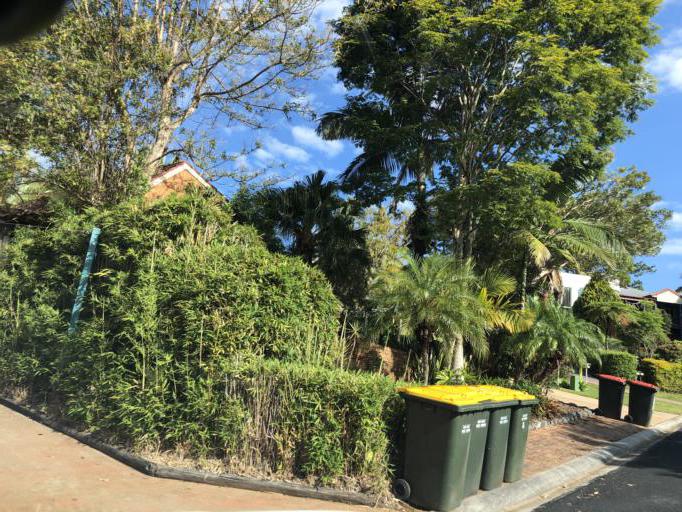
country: AU
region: New South Wales
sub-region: Coffs Harbour
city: Coffs Harbour
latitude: -30.2553
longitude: 153.1328
